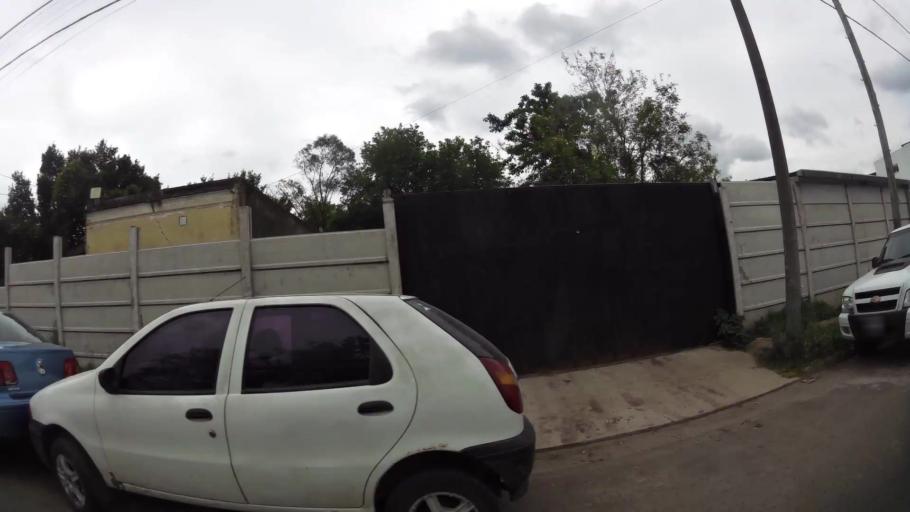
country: AR
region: Buenos Aires
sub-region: Partido de Zarate
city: Zarate
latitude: -34.1090
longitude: -59.0156
